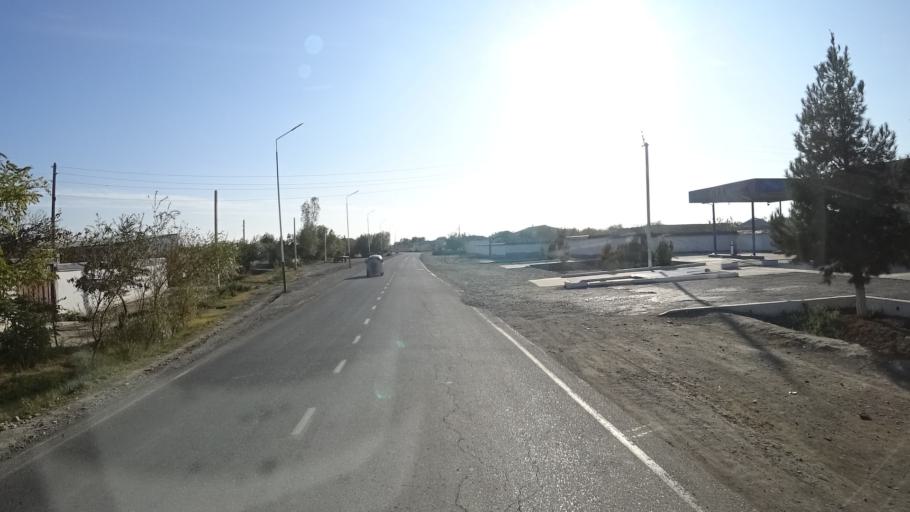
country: UZ
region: Navoiy
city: Beshrabot
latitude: 40.2105
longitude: 65.3853
